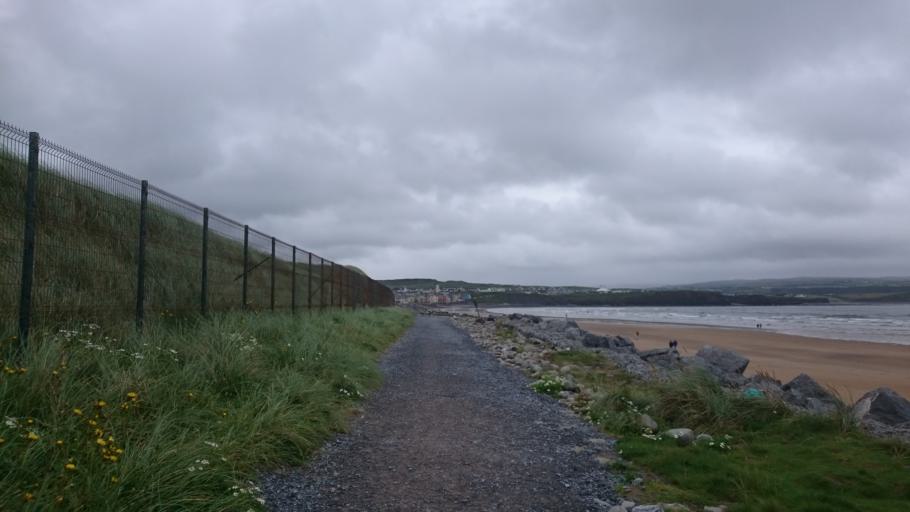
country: IE
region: Munster
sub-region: An Clar
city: Kilrush
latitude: 52.9386
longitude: -9.3557
